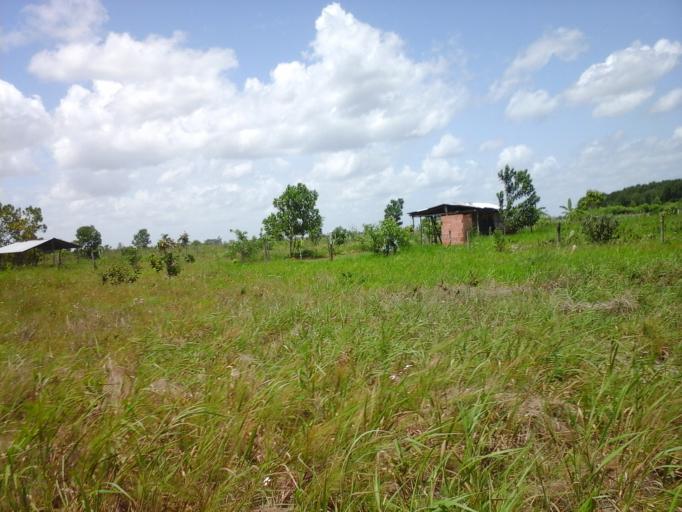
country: CO
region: Cundinamarca
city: Tibacuy
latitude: 4.2259
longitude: -72.4644
